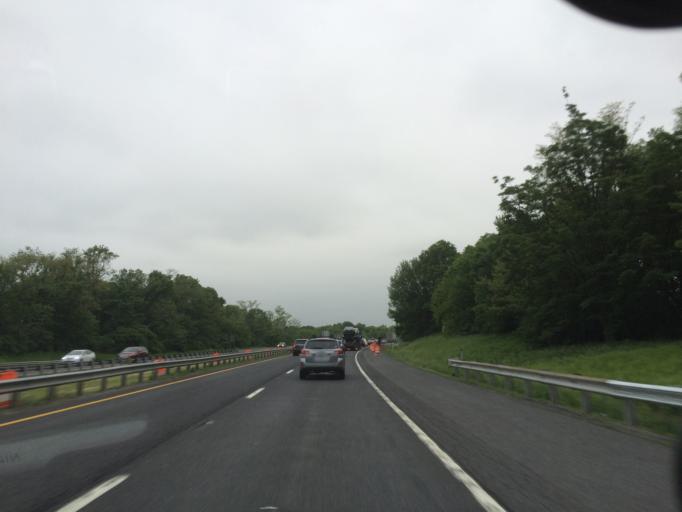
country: US
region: Maryland
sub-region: Washington County
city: Halfway
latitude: 39.6069
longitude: -77.7743
